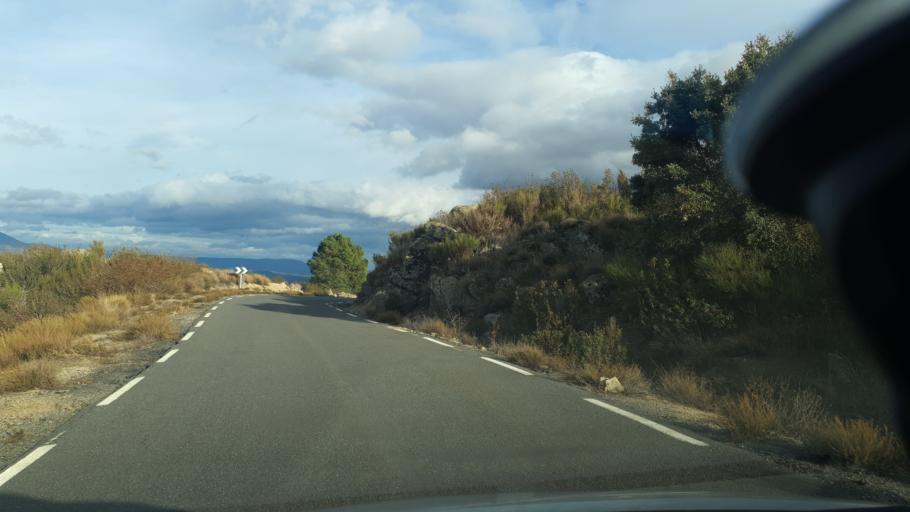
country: ES
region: Castille and Leon
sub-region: Provincia de Avila
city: Navatalgordo
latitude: 40.4112
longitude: -4.8286
